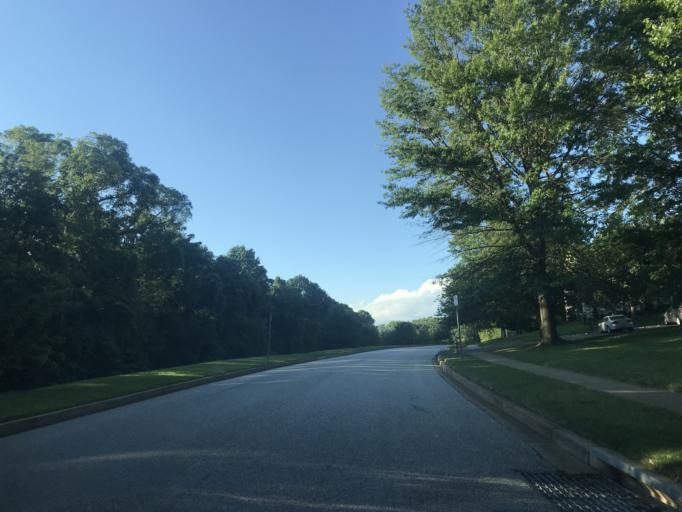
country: US
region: Maryland
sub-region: Harford County
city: South Bel Air
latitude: 39.5589
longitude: -76.3261
